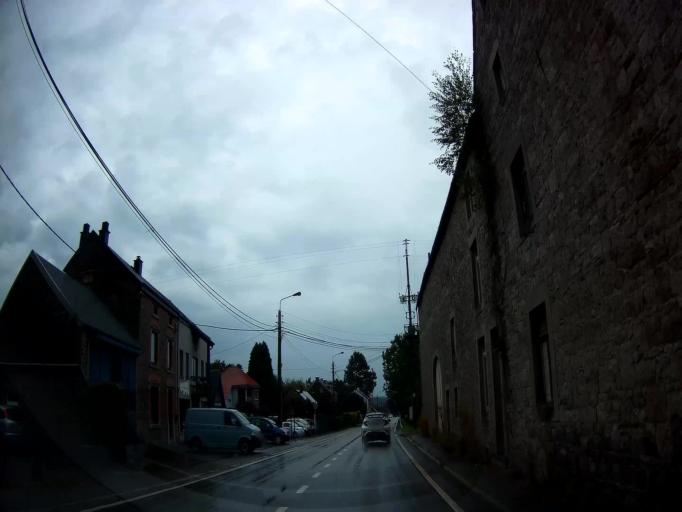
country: BE
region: Wallonia
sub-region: Province de Liege
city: Aywaille
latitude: 50.4609
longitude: 5.6528
